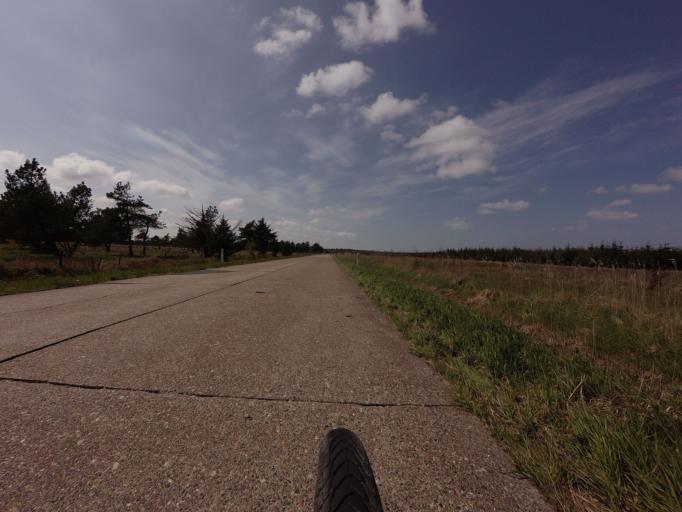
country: DK
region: North Denmark
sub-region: Jammerbugt Kommune
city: Brovst
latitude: 57.1644
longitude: 9.5011
